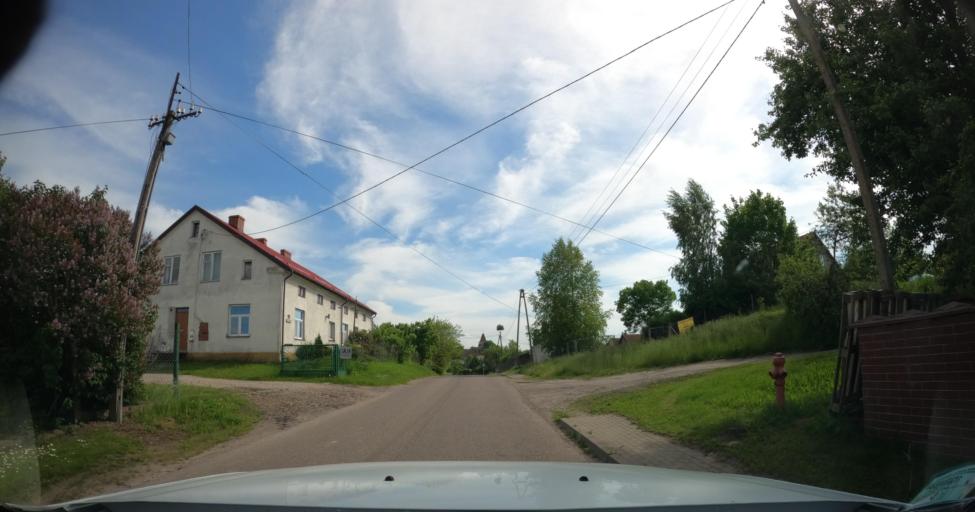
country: PL
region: Warmian-Masurian Voivodeship
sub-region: Powiat lidzbarski
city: Lubomino
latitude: 54.0714
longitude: 20.2396
